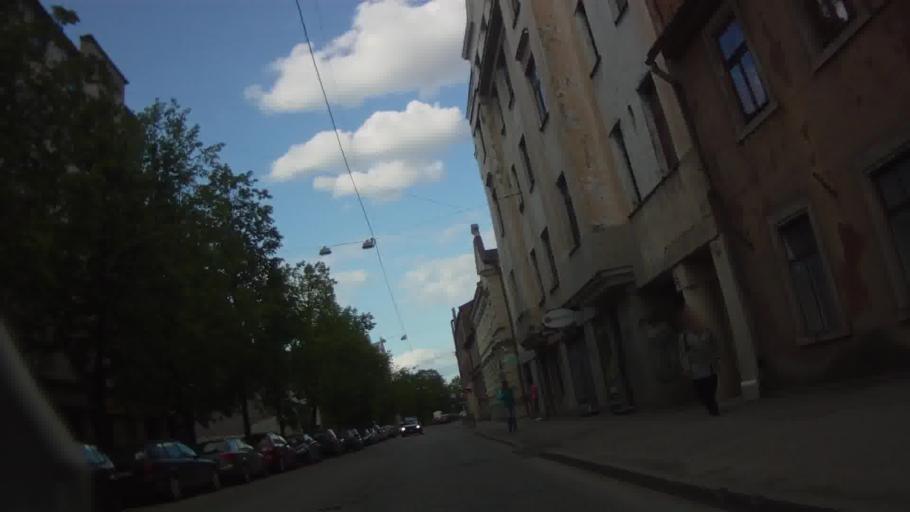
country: LV
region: Riga
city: Riga
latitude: 56.9645
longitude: 24.1385
